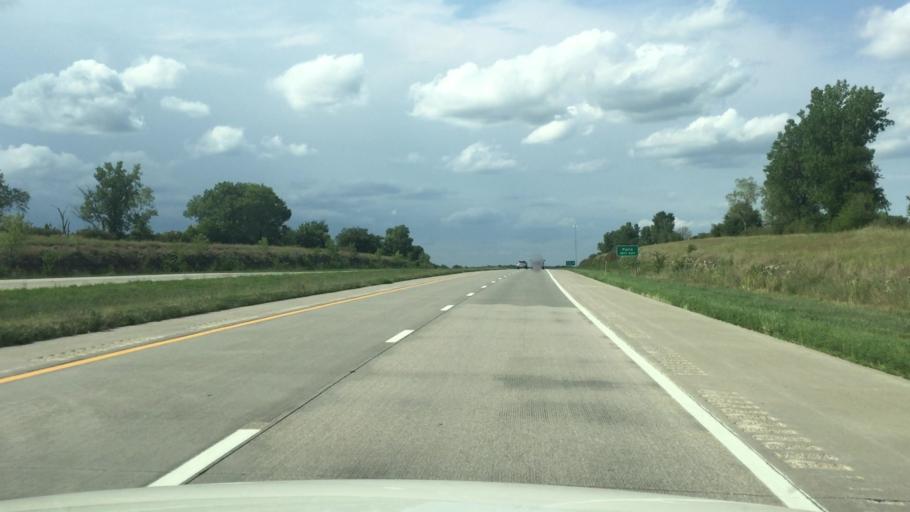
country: US
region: Kansas
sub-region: Miami County
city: Louisburg
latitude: 38.5552
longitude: -94.6907
